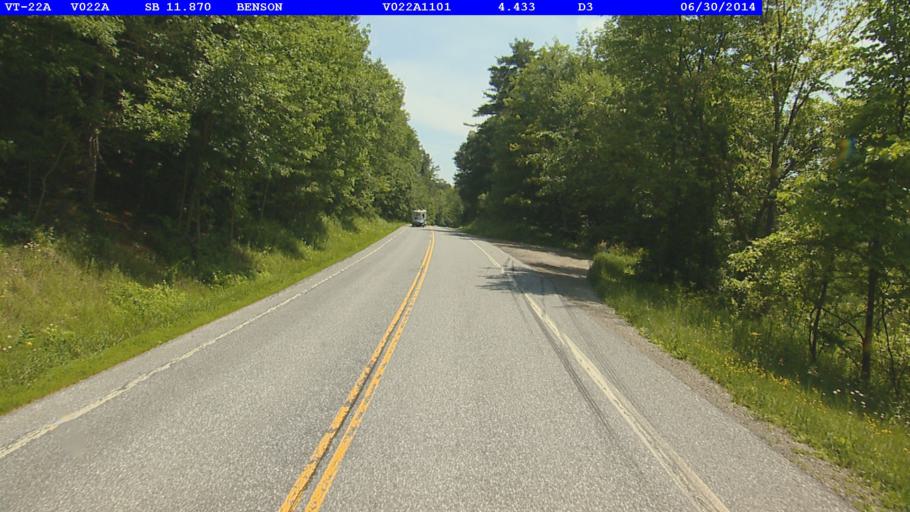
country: US
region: Vermont
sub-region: Rutland County
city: Fair Haven
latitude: 43.7316
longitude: -73.3039
